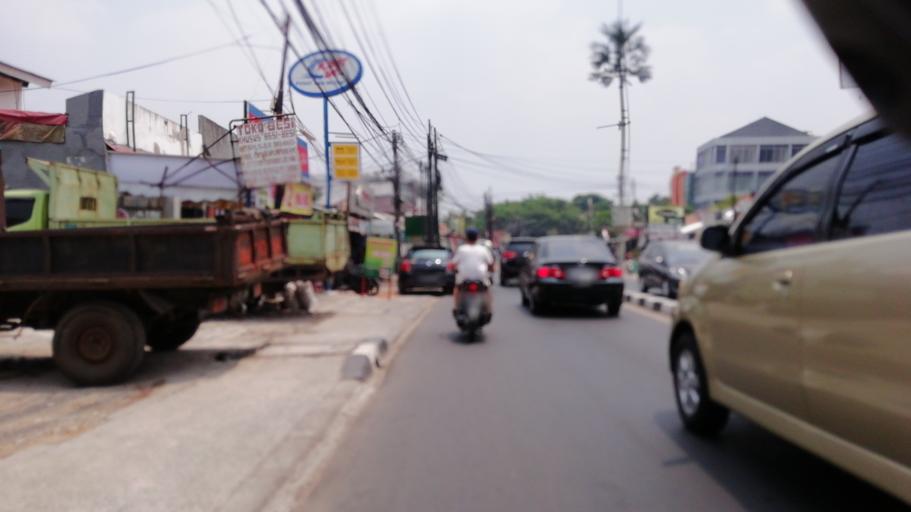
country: ID
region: West Java
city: Pamulang
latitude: -6.3026
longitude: 106.7946
